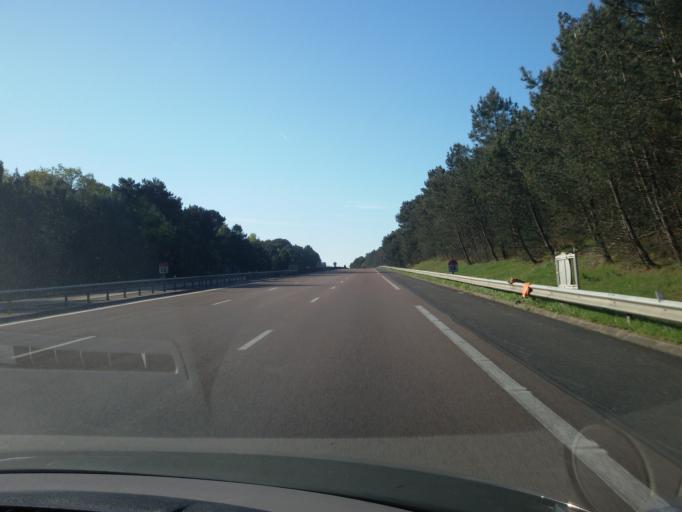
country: FR
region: Ile-de-France
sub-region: Departement de Seine-et-Marne
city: Arbonne-la-Foret
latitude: 48.3862
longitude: 2.5572
